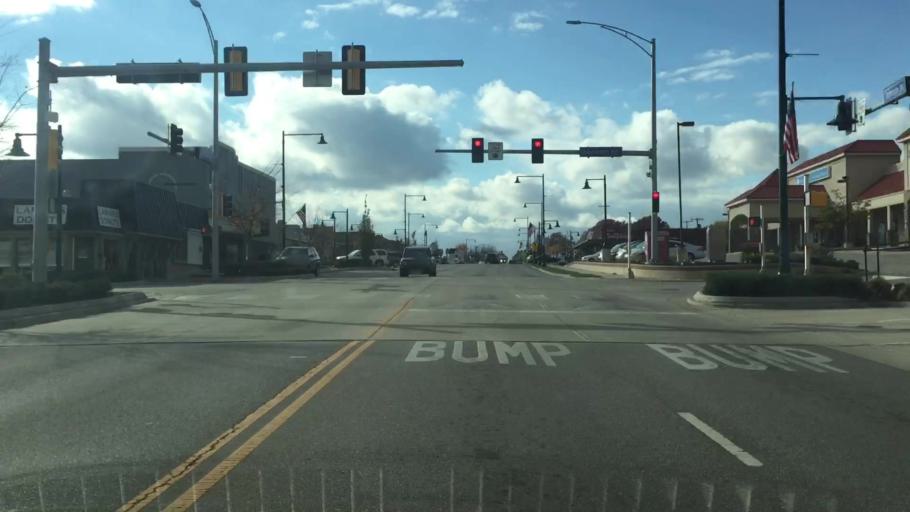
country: US
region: Kansas
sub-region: Johnson County
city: Mission
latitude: 39.0221
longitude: -94.6533
